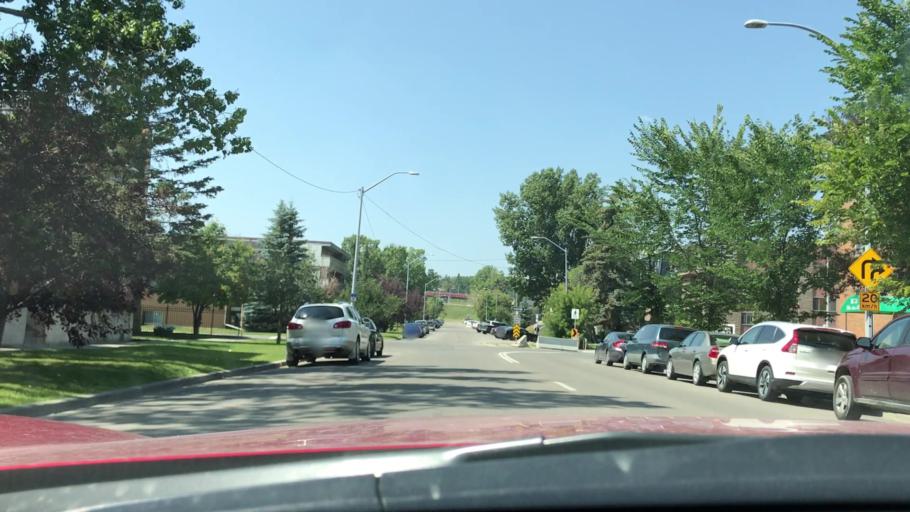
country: CA
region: Alberta
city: Calgary
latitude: 51.0435
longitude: -114.1034
